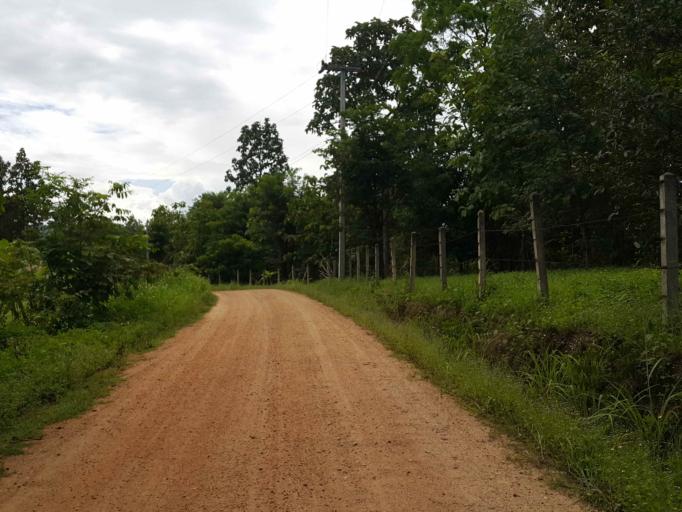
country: TH
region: Chiang Mai
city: San Sai
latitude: 18.9469
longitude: 98.9115
